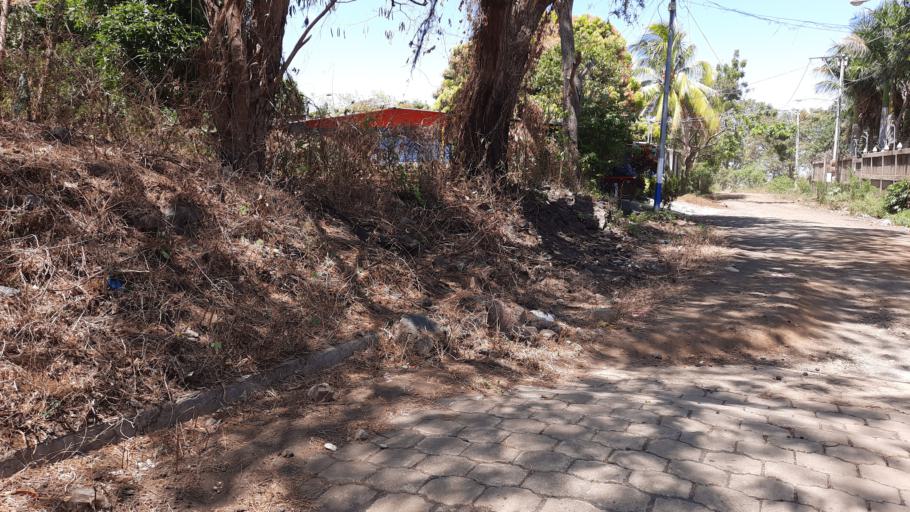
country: NI
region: Masaya
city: Ticuantepe
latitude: 12.0265
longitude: -86.1674
